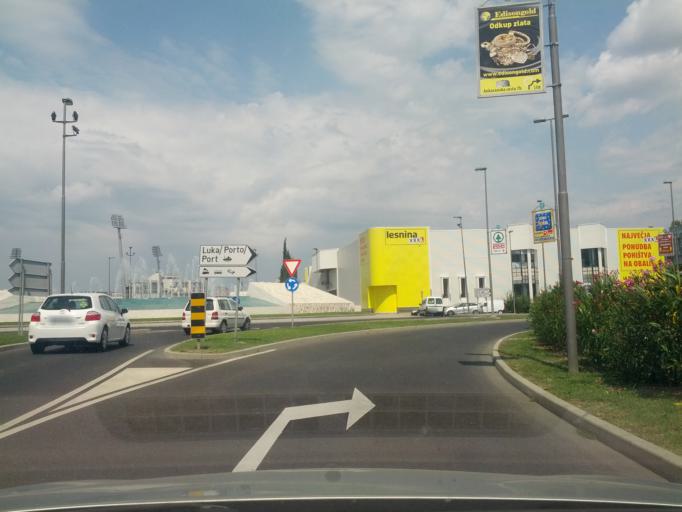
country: SI
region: Koper-Capodistria
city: Koper
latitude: 45.5401
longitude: 13.7332
